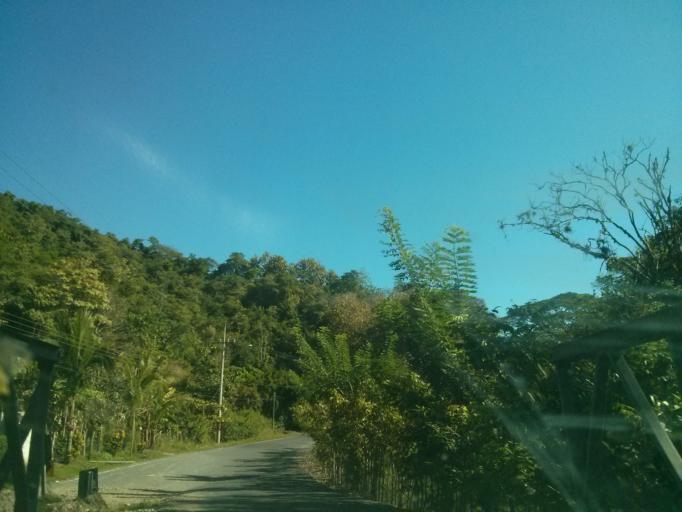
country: CR
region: Puntarenas
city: Paquera
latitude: 9.7775
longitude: -84.9549
